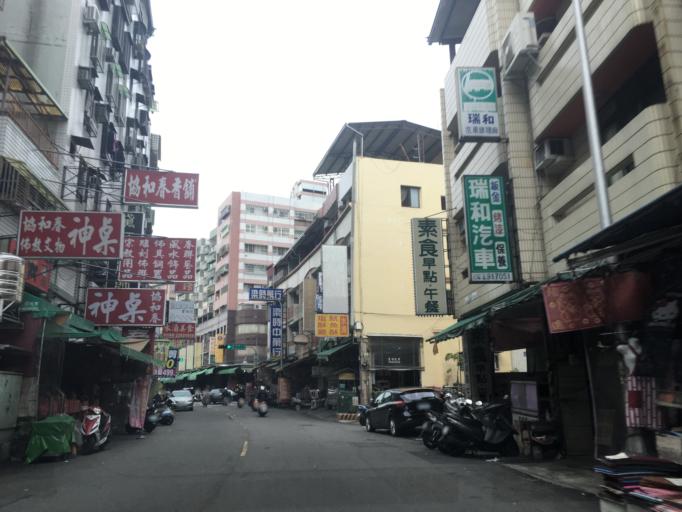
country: TW
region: Taiwan
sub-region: Taichung City
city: Taichung
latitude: 24.1746
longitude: 120.6663
